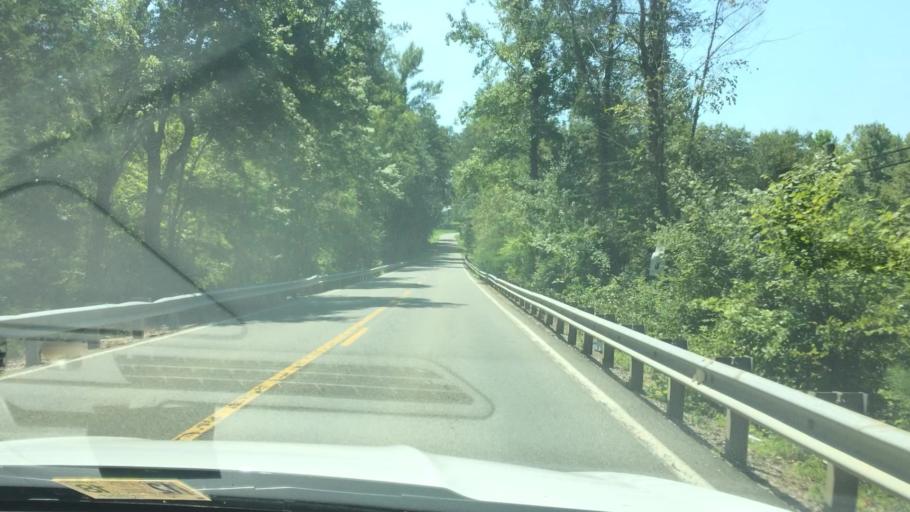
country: US
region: Virginia
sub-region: Charles City County
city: Charles City
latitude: 37.4007
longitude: -77.0480
